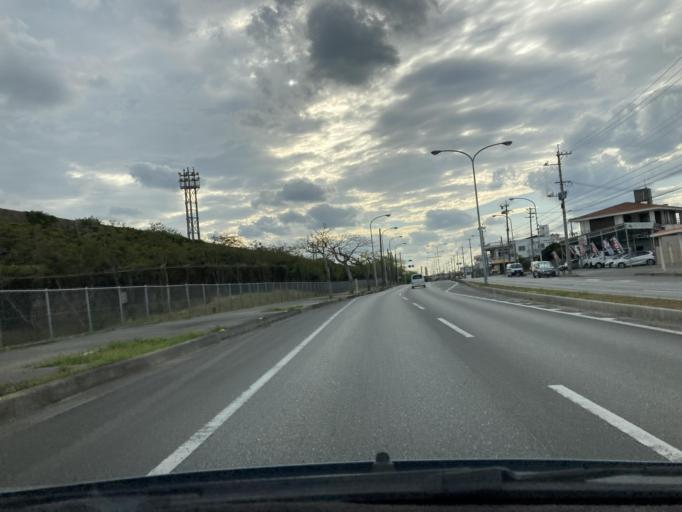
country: JP
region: Okinawa
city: Okinawa
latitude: 26.3656
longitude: 127.7712
